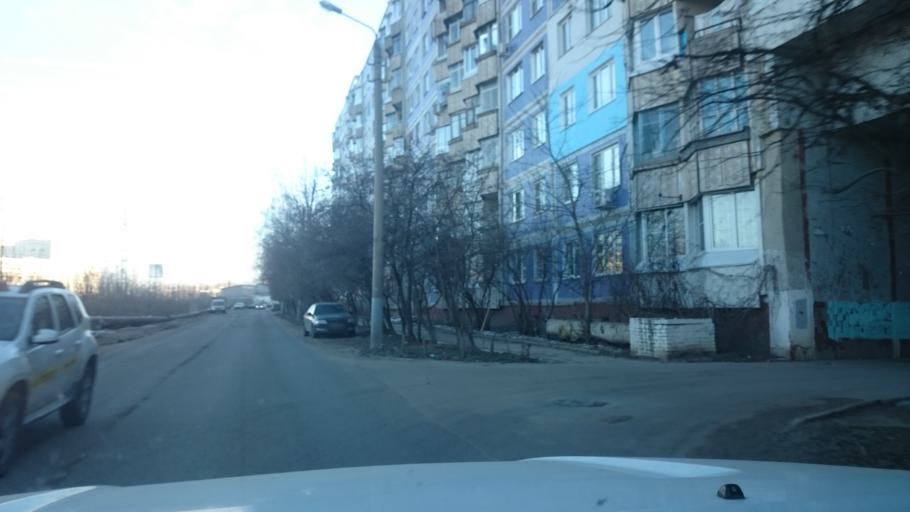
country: RU
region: Tula
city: Tula
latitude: 54.2082
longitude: 37.6824
